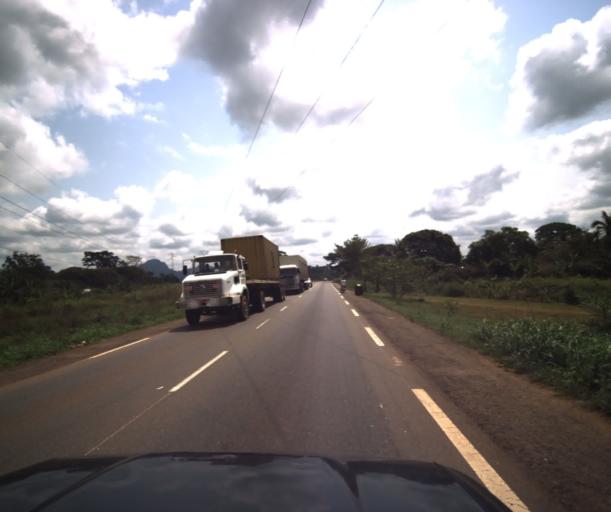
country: CM
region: Centre
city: Eseka
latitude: 3.8918
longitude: 10.7745
